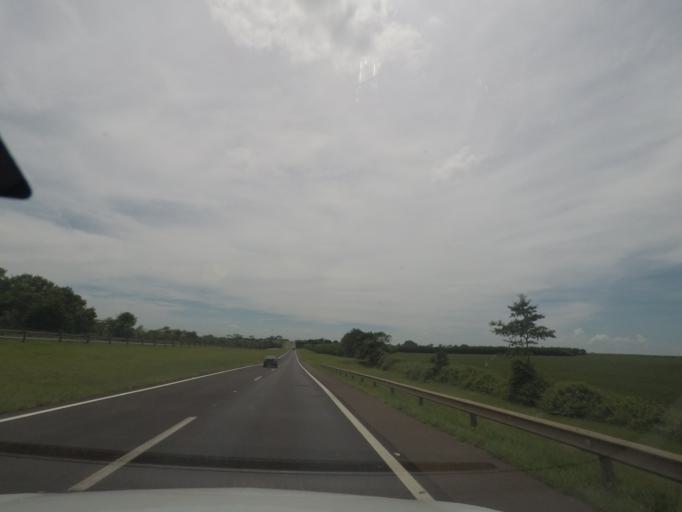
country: BR
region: Sao Paulo
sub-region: Bebedouro
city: Bebedouro
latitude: -20.9806
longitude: -48.4368
